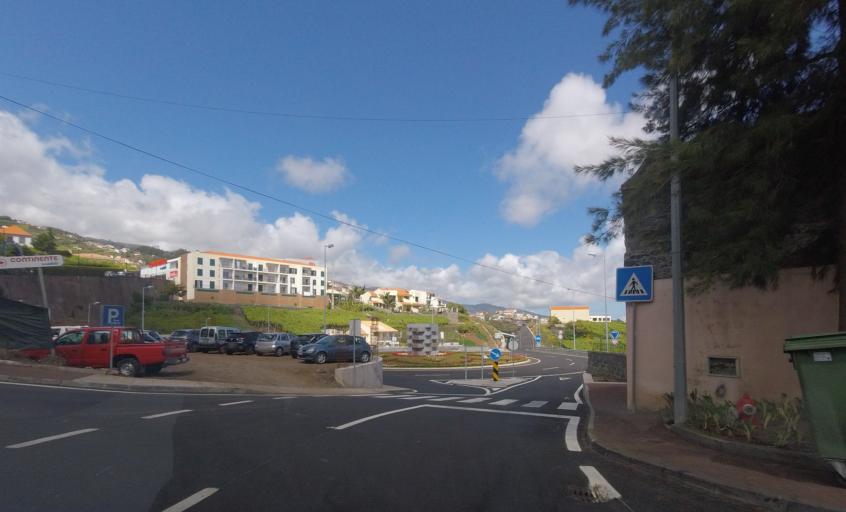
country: PT
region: Madeira
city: Camara de Lobos
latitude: 32.6684
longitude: -16.9786
